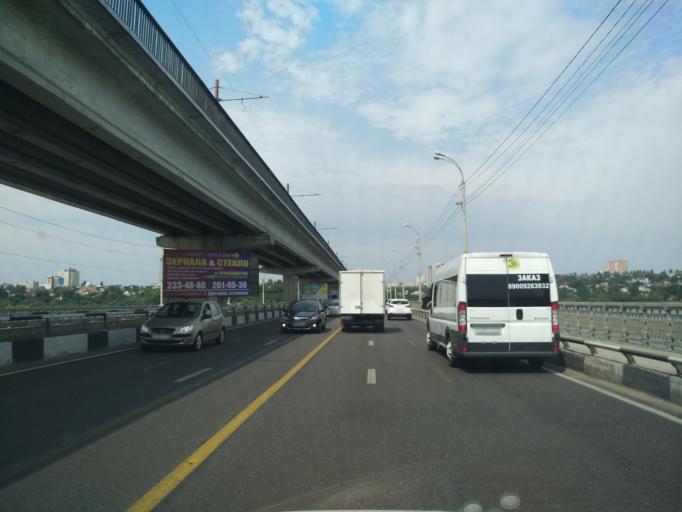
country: RU
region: Voronezj
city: Voronezh
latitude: 51.6912
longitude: 39.2430
